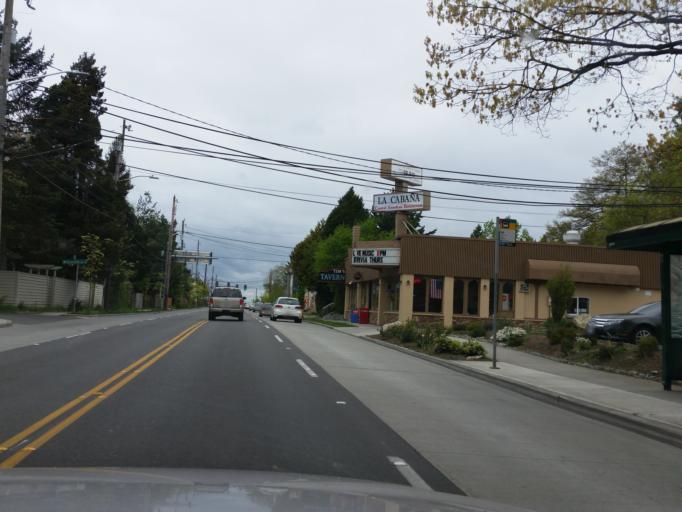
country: US
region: Washington
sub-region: King County
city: Shoreline
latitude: 47.7051
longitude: -122.3503
